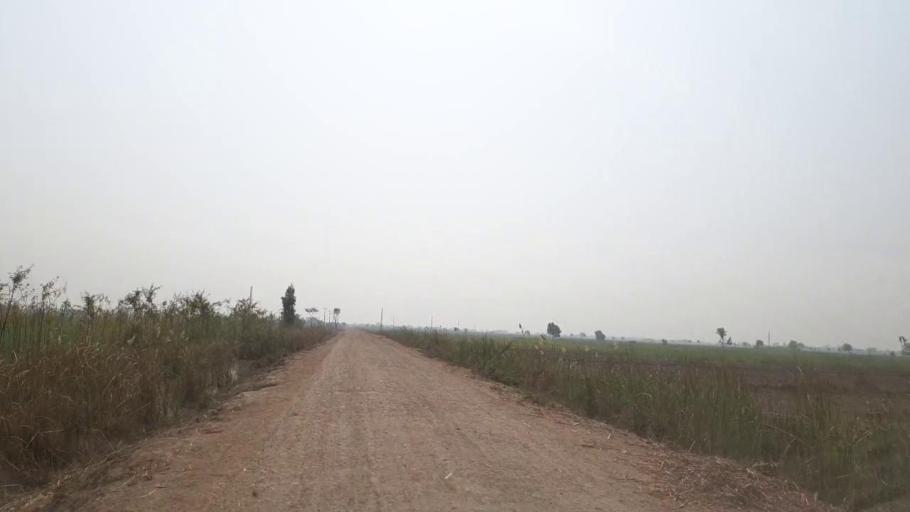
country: PK
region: Sindh
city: Mirpur Khas
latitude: 25.5487
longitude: 69.0586
